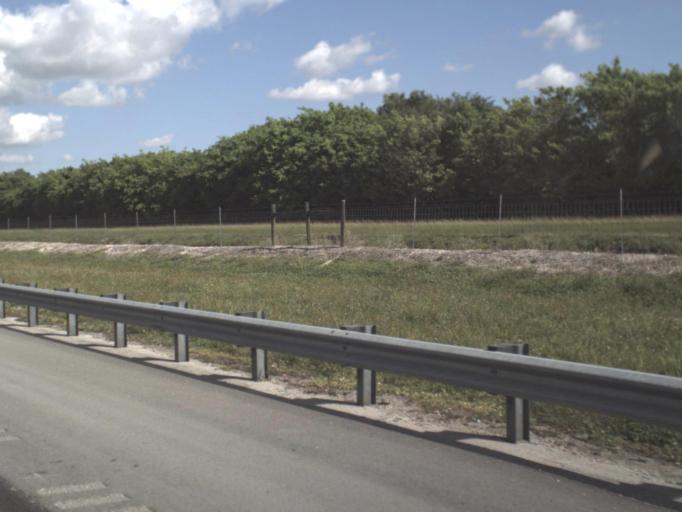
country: US
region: Florida
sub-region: Palm Beach County
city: Boca Del Mar
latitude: 26.3949
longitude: -80.1710
